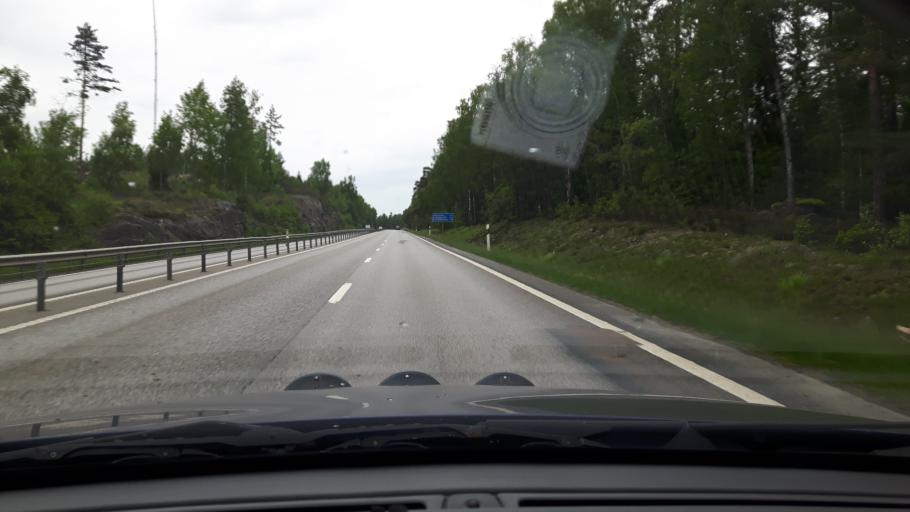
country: SE
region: OEstergoetland
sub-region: Norrkopings Kommun
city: Jursla
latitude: 58.7444
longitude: 16.1740
